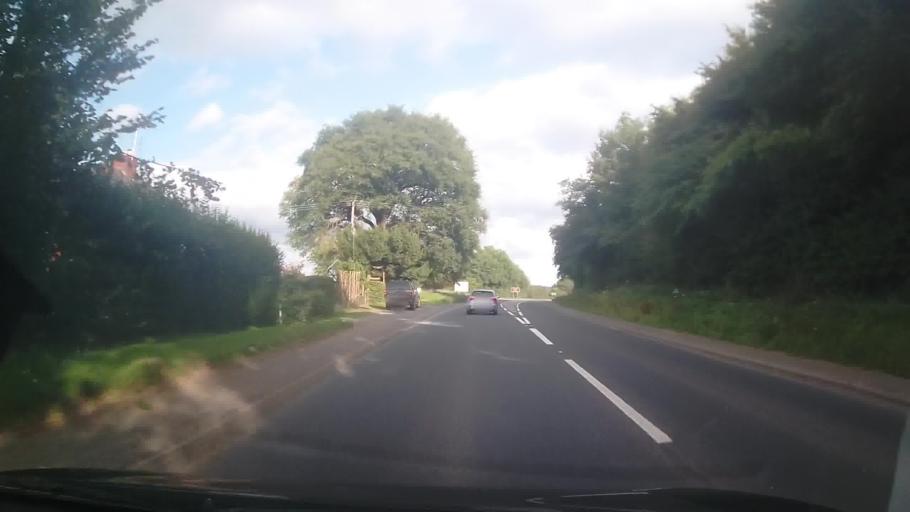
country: GB
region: England
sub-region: Shropshire
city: Bromfield
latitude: 52.3889
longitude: -2.7449
